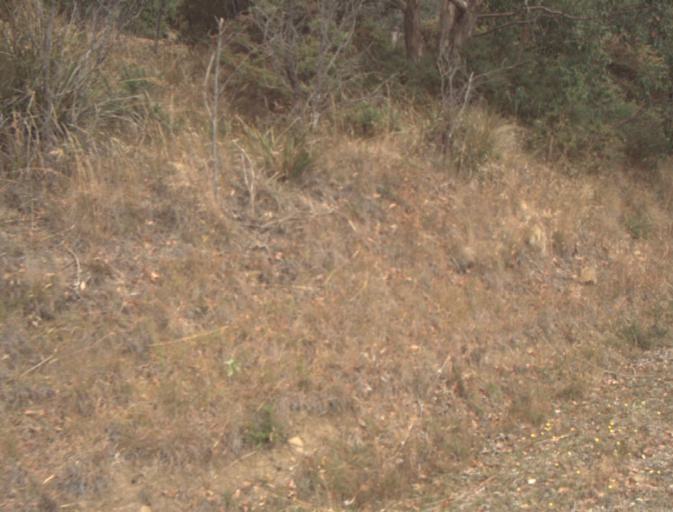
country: AU
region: Tasmania
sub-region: Northern Midlands
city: Evandale
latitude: -41.4976
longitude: 147.4089
